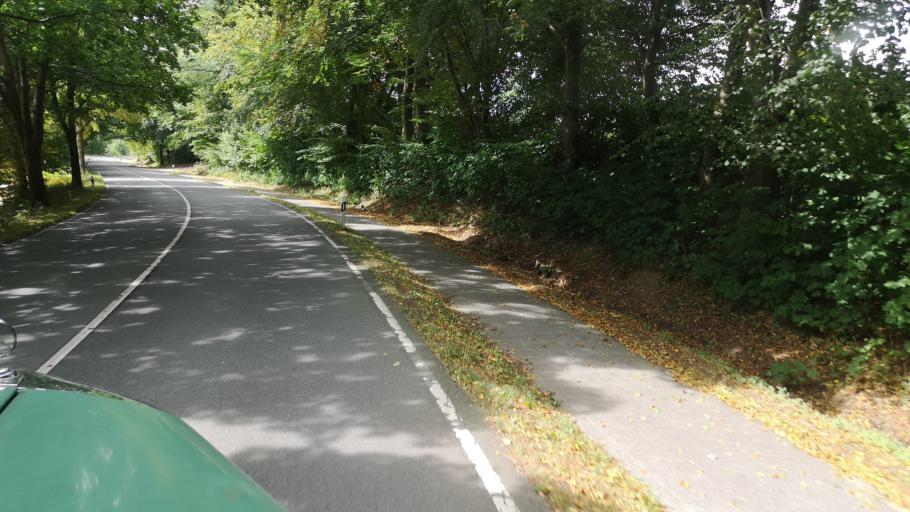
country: DE
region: North Rhine-Westphalia
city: Huckeswagen
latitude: 51.1569
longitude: 7.3518
